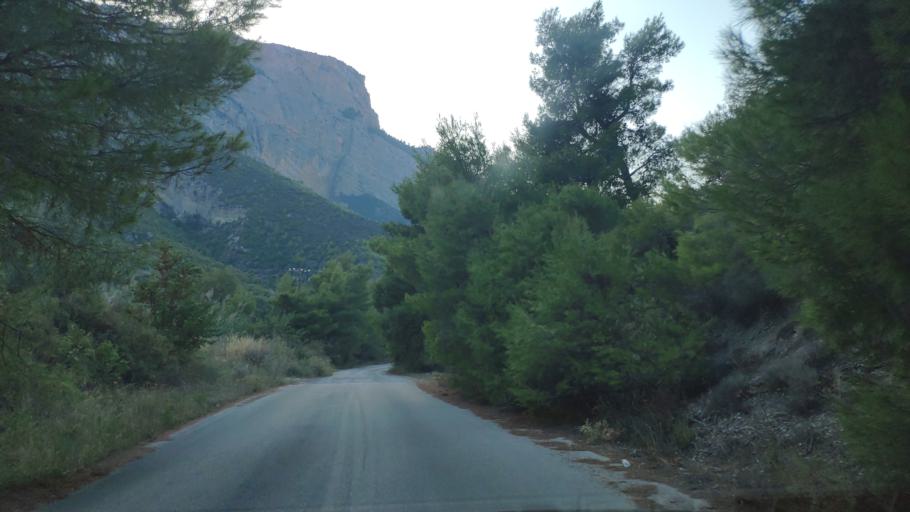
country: GR
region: West Greece
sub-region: Nomos Achaias
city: Aiyira
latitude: 38.0989
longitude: 22.4018
